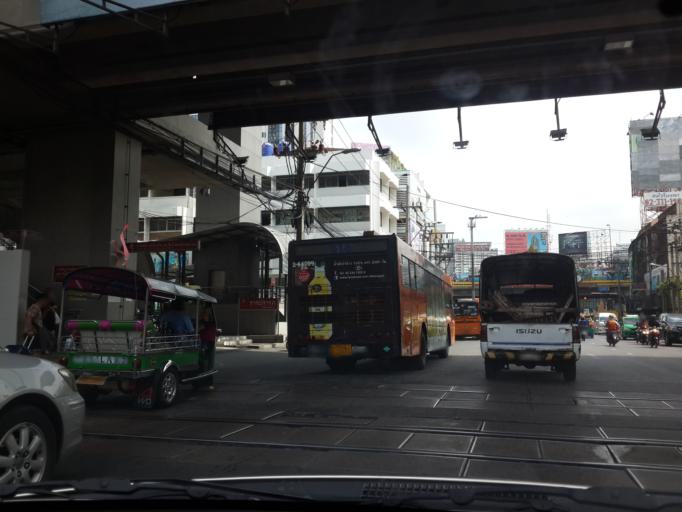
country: TH
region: Bangkok
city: Ratchathewi
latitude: 13.7549
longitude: 100.5422
